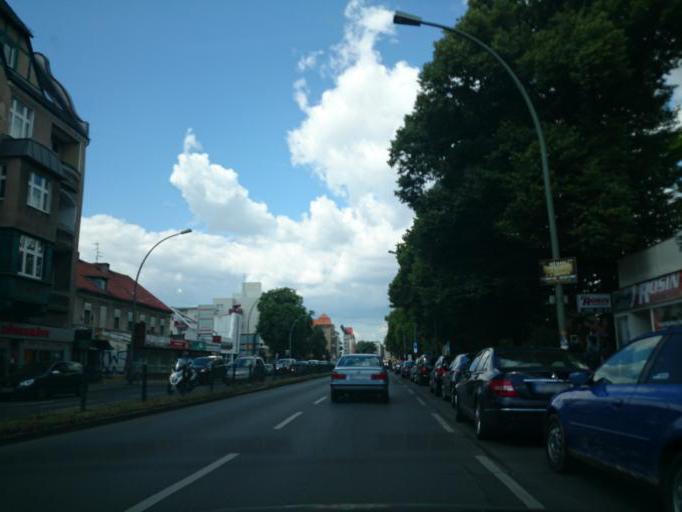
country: DE
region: Berlin
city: Mariendorf
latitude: 52.4405
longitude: 13.3873
